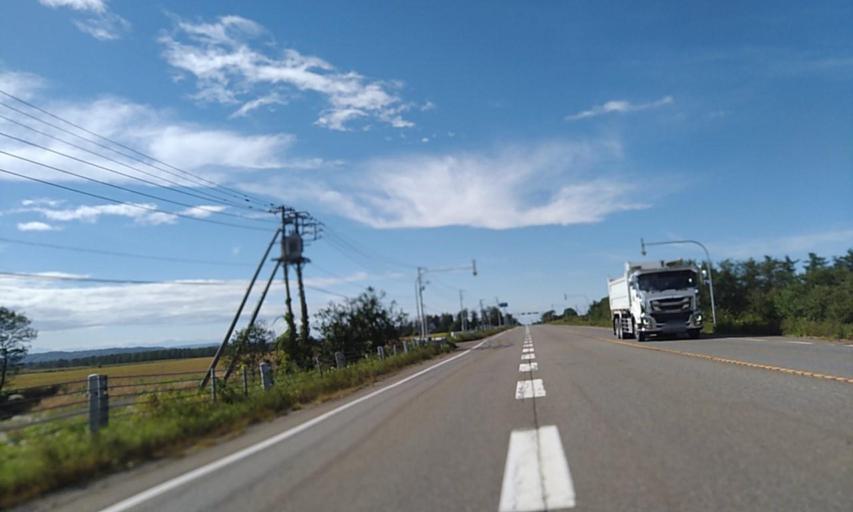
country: JP
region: Hokkaido
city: Obihiro
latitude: 42.7988
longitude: 143.5735
